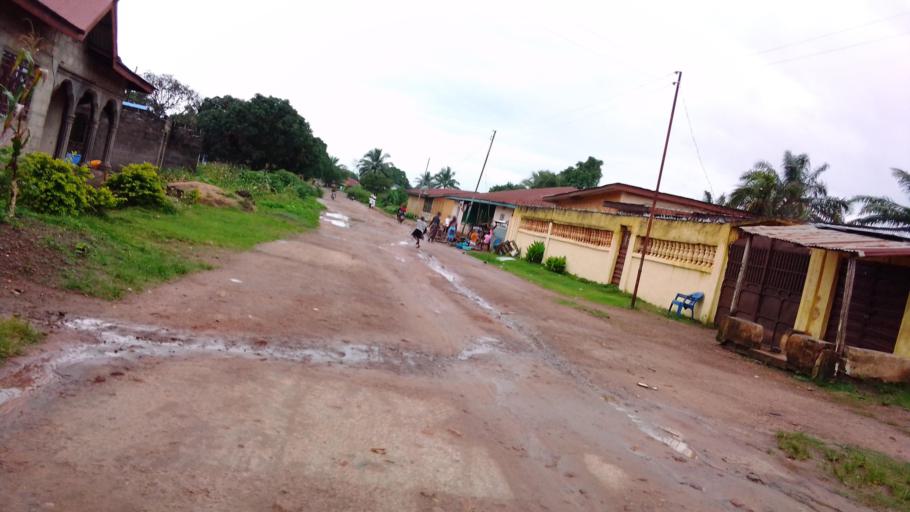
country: SL
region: Eastern Province
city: Kenema
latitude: 7.8983
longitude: -11.1795
